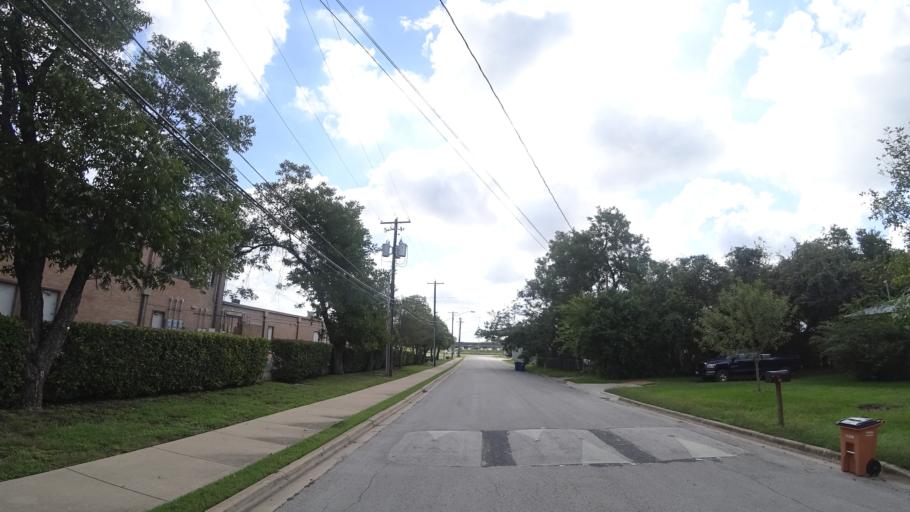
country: US
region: Texas
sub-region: Travis County
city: Austin
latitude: 30.3470
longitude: -97.7150
